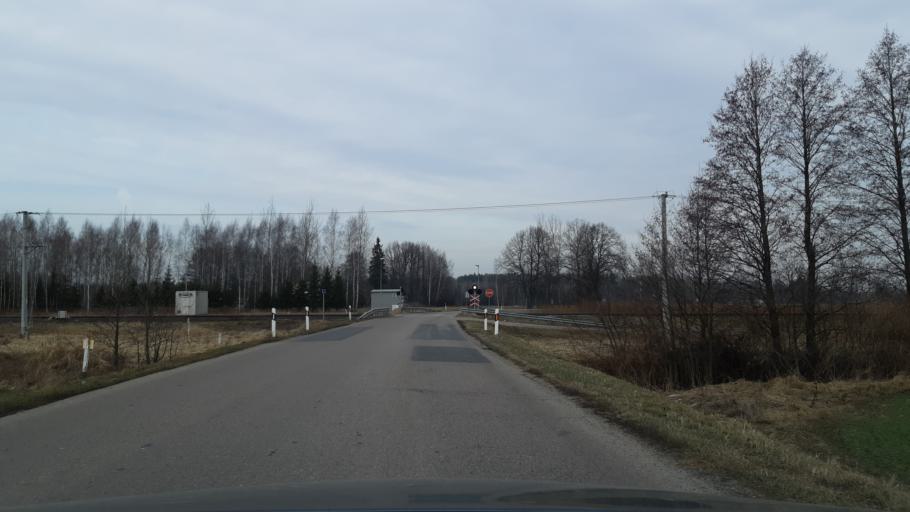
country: LT
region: Marijampoles apskritis
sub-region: Marijampole Municipality
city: Marijampole
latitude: 54.7264
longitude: 23.3363
